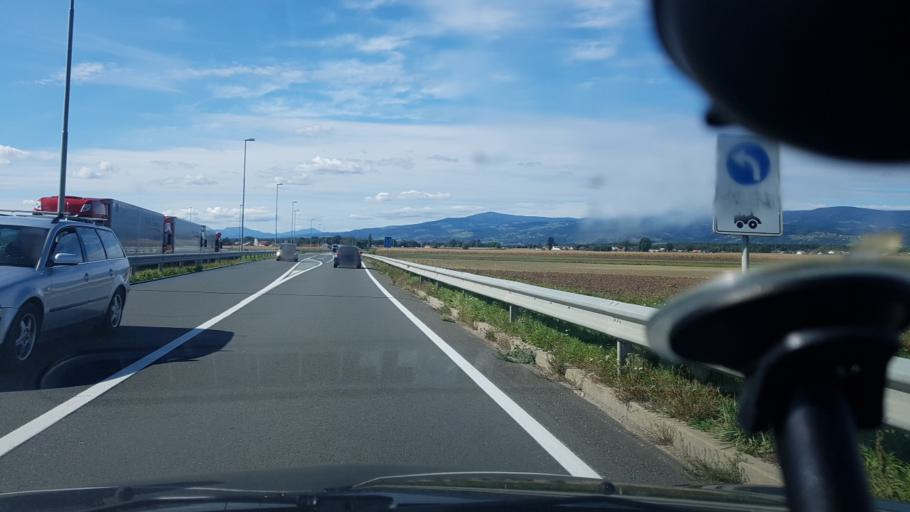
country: SI
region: Slovenska Bistrica
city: Pragersko
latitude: 46.4084
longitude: 15.7088
